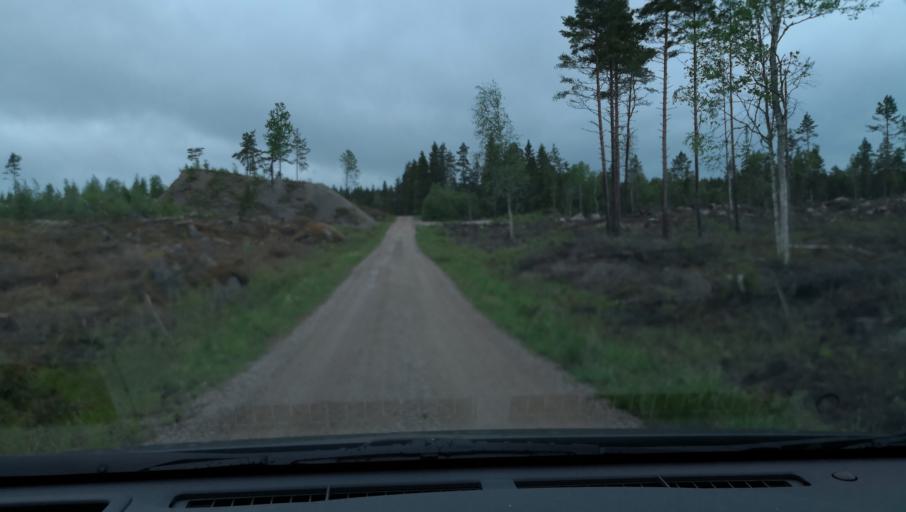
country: SE
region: Uppsala
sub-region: Enkopings Kommun
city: Orsundsbro
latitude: 59.9406
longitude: 17.3123
